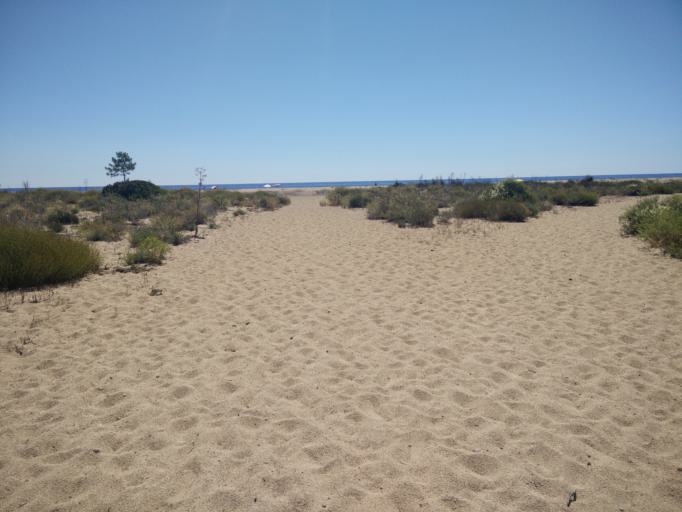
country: FR
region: Corsica
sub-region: Departement de la Corse-du-Sud
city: Sari-Solenzara
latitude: 41.7081
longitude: 9.4007
